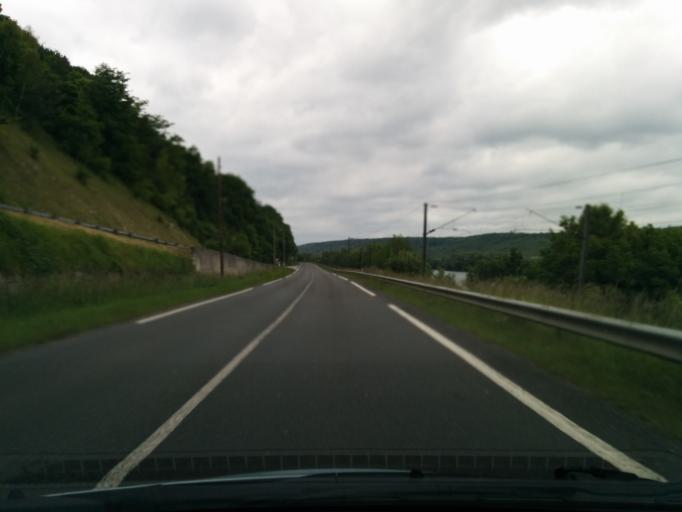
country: FR
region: Ile-de-France
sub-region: Departement des Yvelines
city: Limetz-Villez
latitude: 49.0662
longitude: 1.5202
